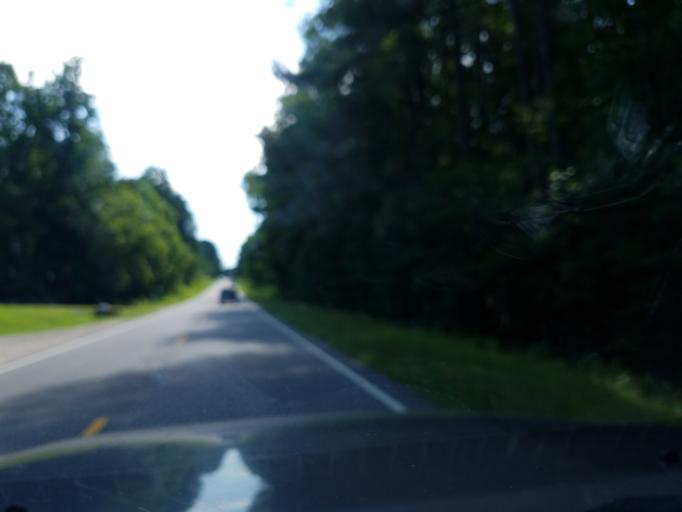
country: US
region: North Carolina
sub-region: Vance County
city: South Henderson
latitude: 36.3307
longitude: -78.4757
